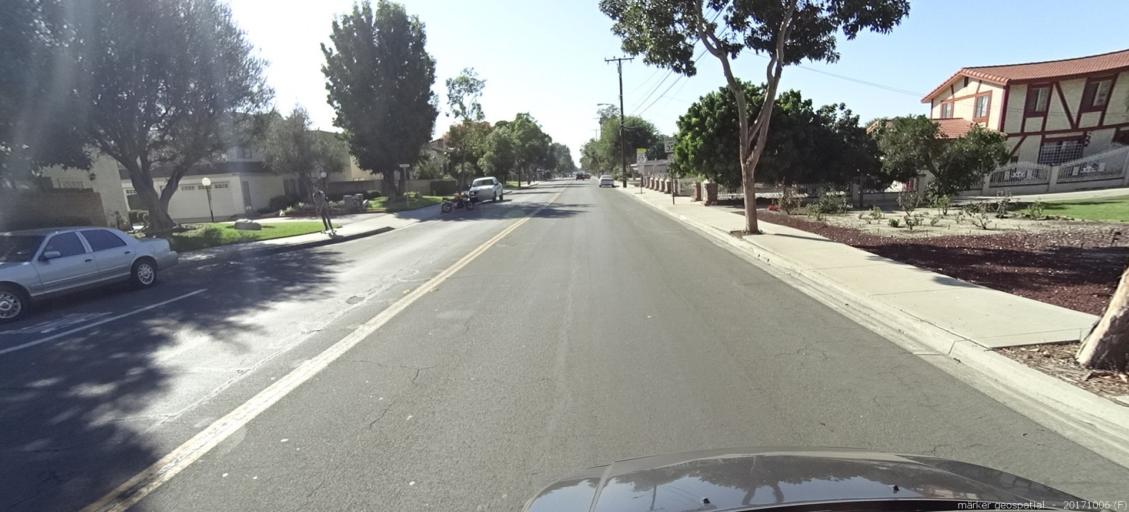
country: US
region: California
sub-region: Orange County
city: Garden Grove
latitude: 33.7815
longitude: -117.9332
